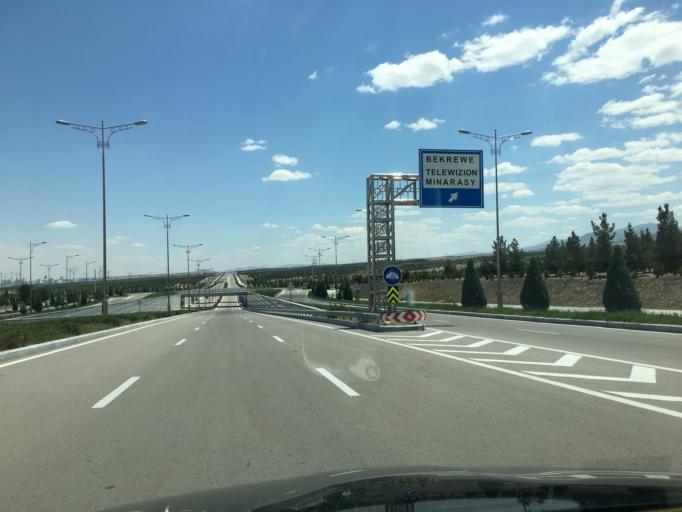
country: TM
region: Ahal
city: Ashgabat
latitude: 37.8802
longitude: 58.2806
